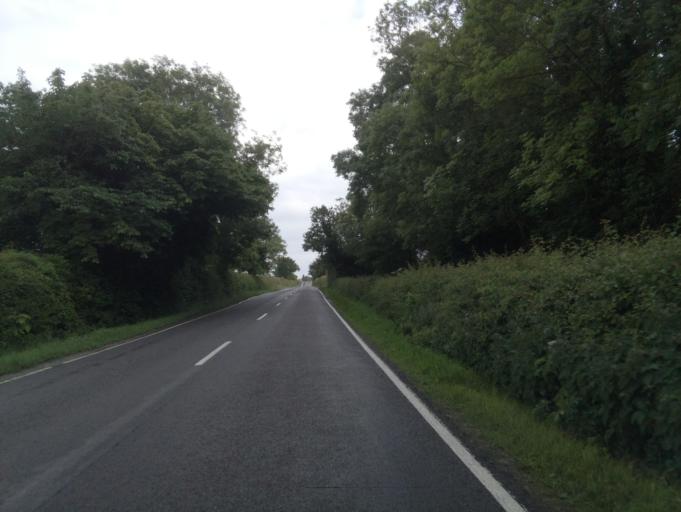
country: GB
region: England
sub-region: Lincolnshire
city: Great Gonerby
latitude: 53.0004
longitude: -0.6683
